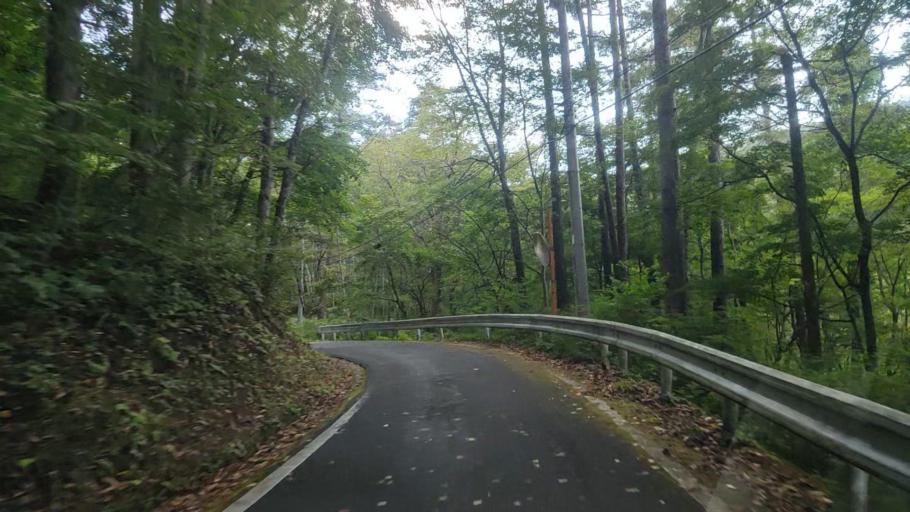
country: JP
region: Gunma
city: Nakanojomachi
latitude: 36.6541
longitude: 138.6348
